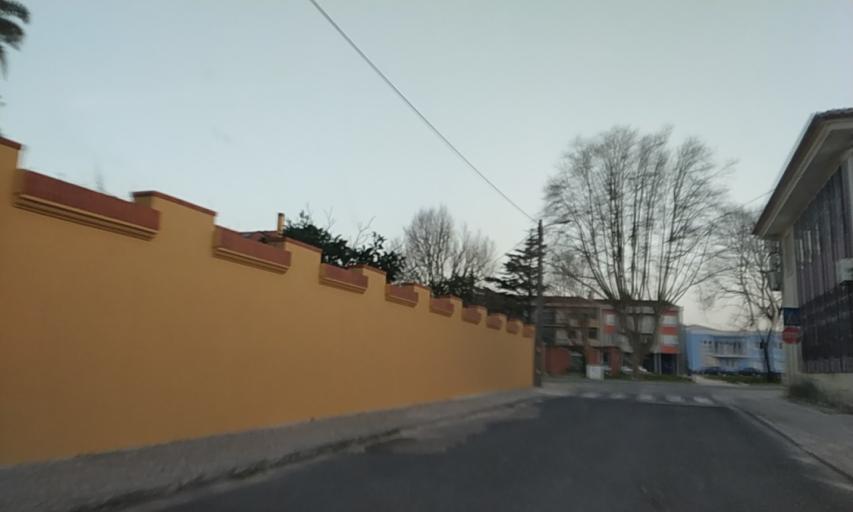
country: PT
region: Leiria
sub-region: Marinha Grande
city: Marinha Grande
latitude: 39.7518
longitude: -8.9291
